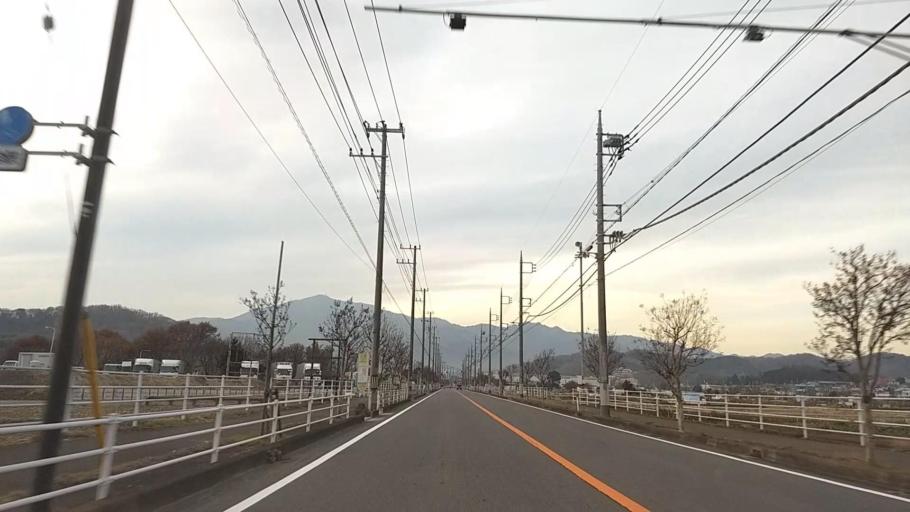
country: JP
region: Kanagawa
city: Atsugi
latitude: 35.4295
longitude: 139.3349
